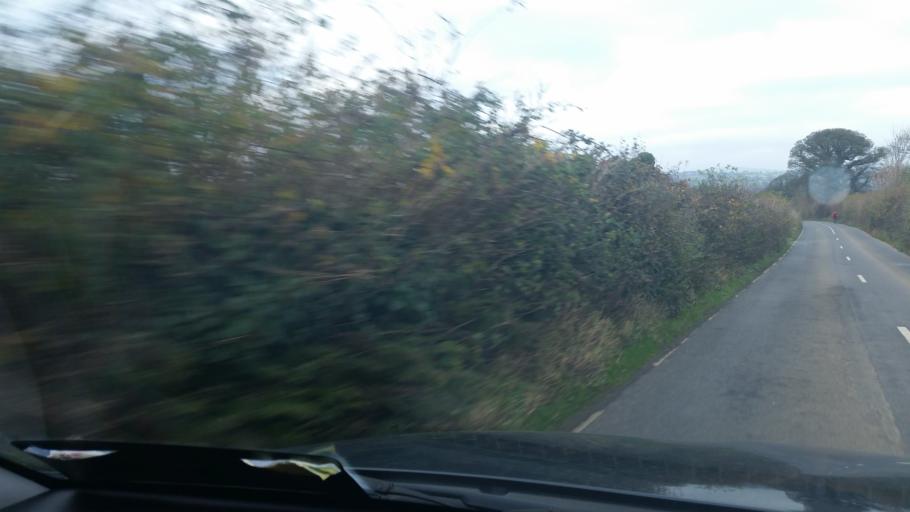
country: IE
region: Leinster
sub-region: Lu
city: Tullyallen
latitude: 53.7068
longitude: -6.4088
